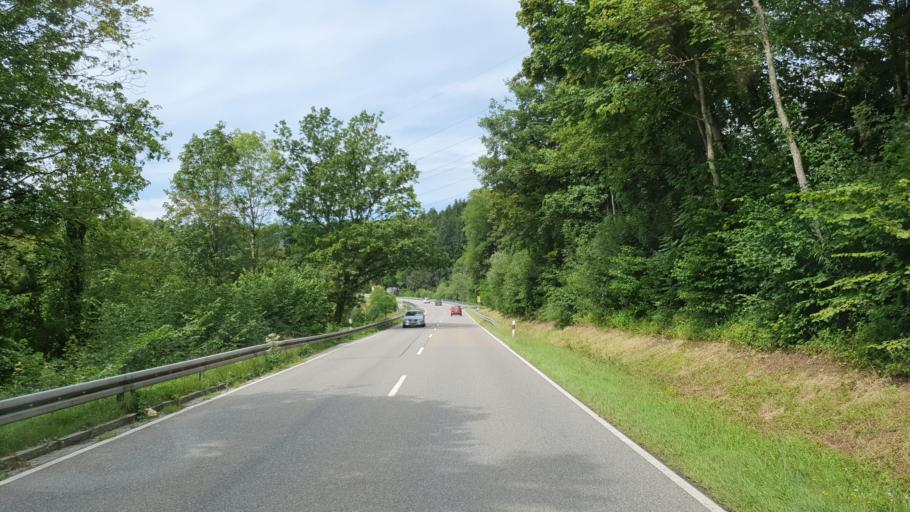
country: AT
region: Vorarlberg
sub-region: Politischer Bezirk Bregenz
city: Hohenweiler
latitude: 47.5957
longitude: 9.7787
